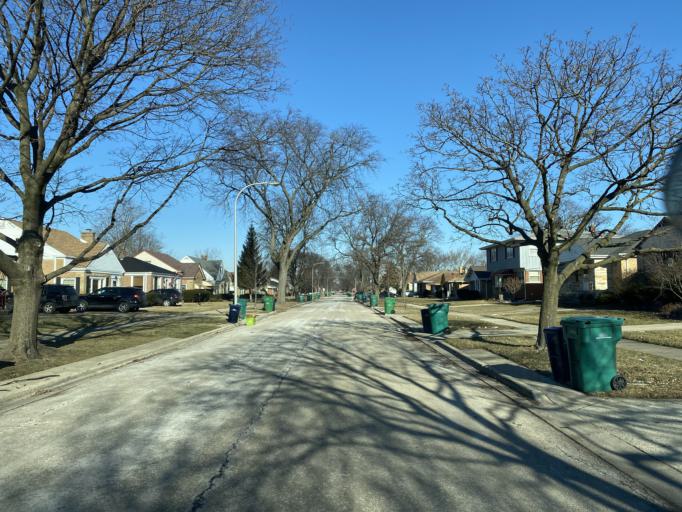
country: US
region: Illinois
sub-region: Cook County
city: Westchester
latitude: 41.8511
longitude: -87.8720
